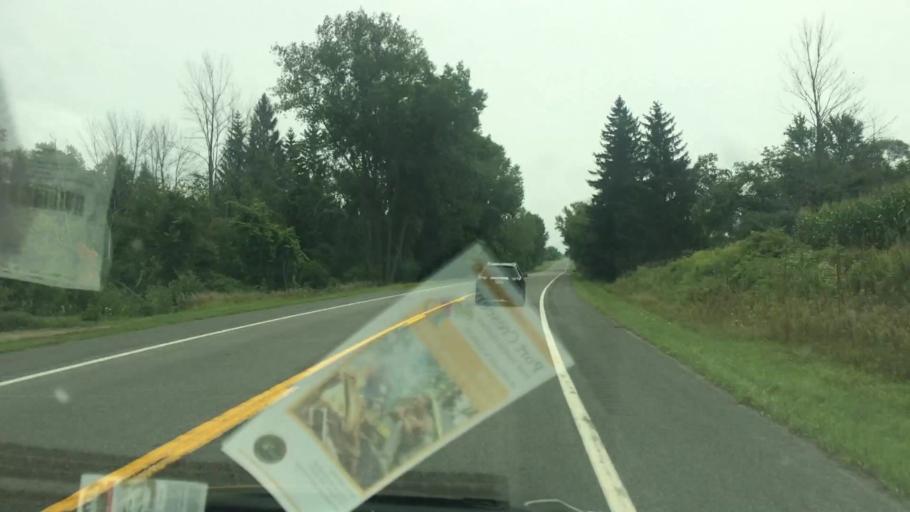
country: US
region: Michigan
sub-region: Huron County
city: Harbor Beach
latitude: 44.0193
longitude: -82.8063
